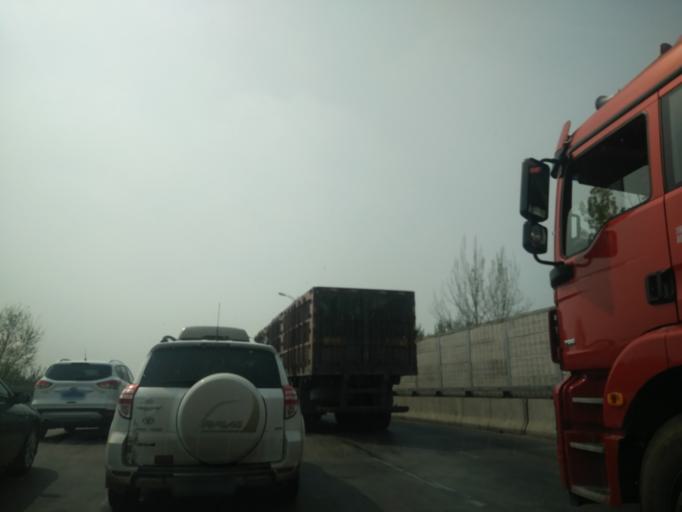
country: CN
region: Beijing
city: Xiji
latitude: 39.7990
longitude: 116.9016
